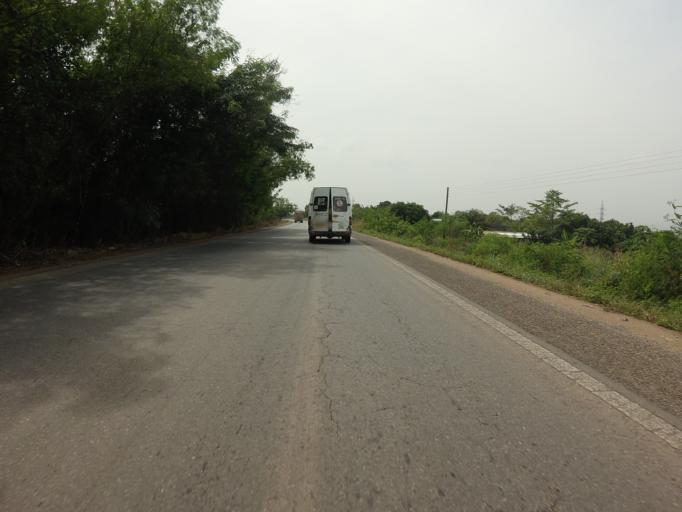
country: GH
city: Akropong
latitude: 6.1092
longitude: 0.0487
